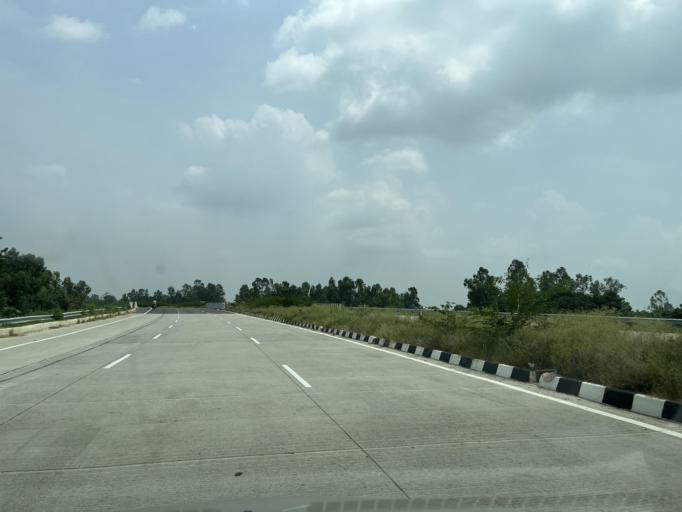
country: IN
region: Uttar Pradesh
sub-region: Bijnor
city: Nagina
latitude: 29.4317
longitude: 78.4047
